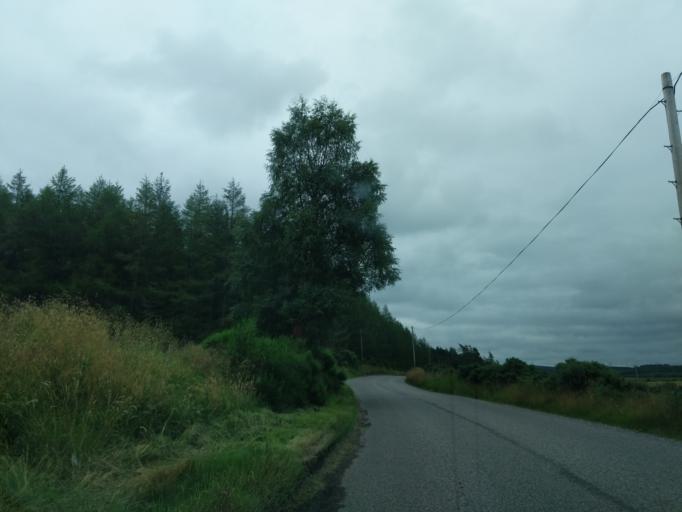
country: GB
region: Scotland
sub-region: Moray
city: Kinloss
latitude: 57.5512
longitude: -3.5155
